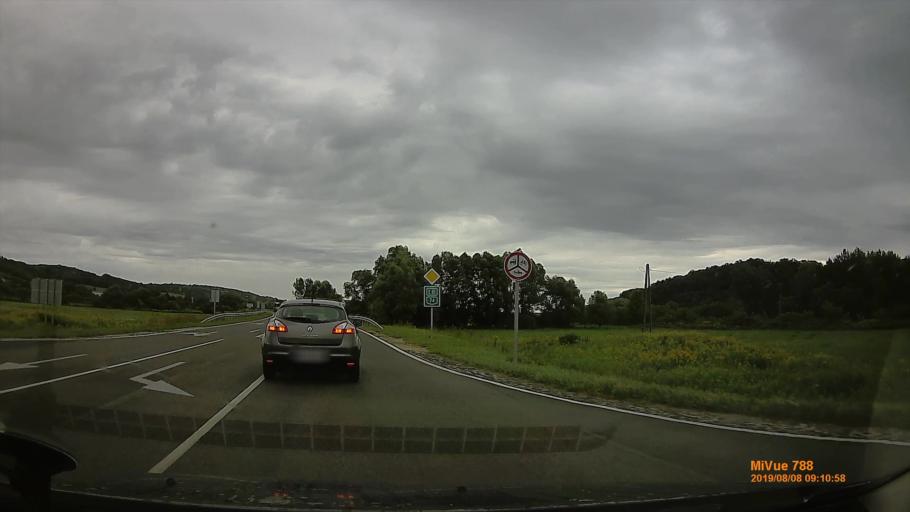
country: HU
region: Zala
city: Zalaegerszeg
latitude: 46.7776
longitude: 16.8579
